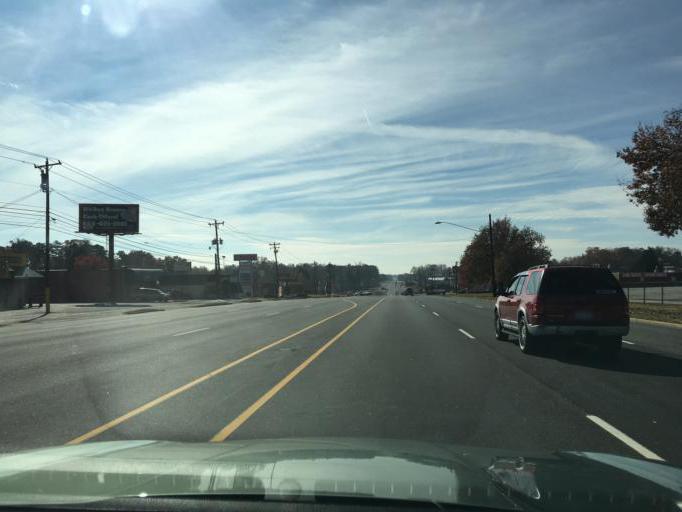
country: US
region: South Carolina
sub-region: Greenville County
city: Wade Hampton
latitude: 34.9033
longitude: -82.3336
